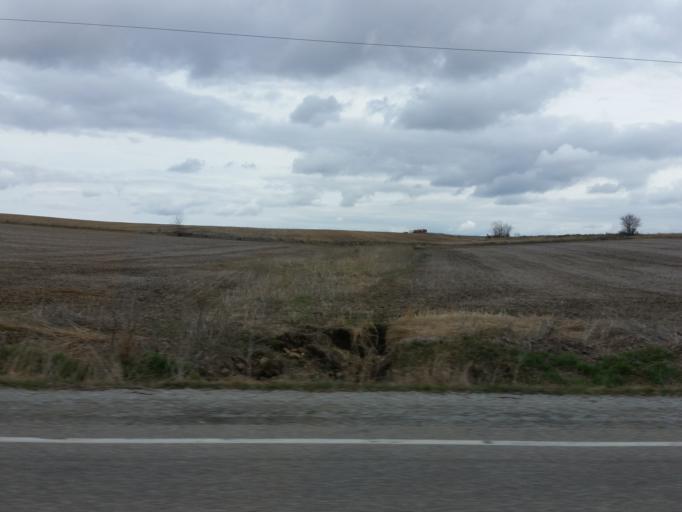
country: US
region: Iowa
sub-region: Black Hawk County
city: Elk Run Heights
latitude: 42.5354
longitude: -92.2191
